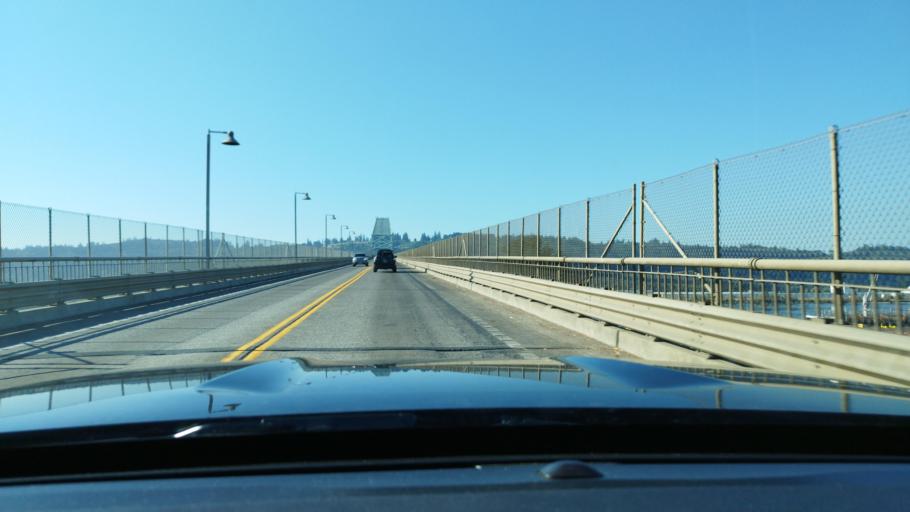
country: US
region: Oregon
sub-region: Columbia County
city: Rainier
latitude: 46.1108
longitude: -122.9552
